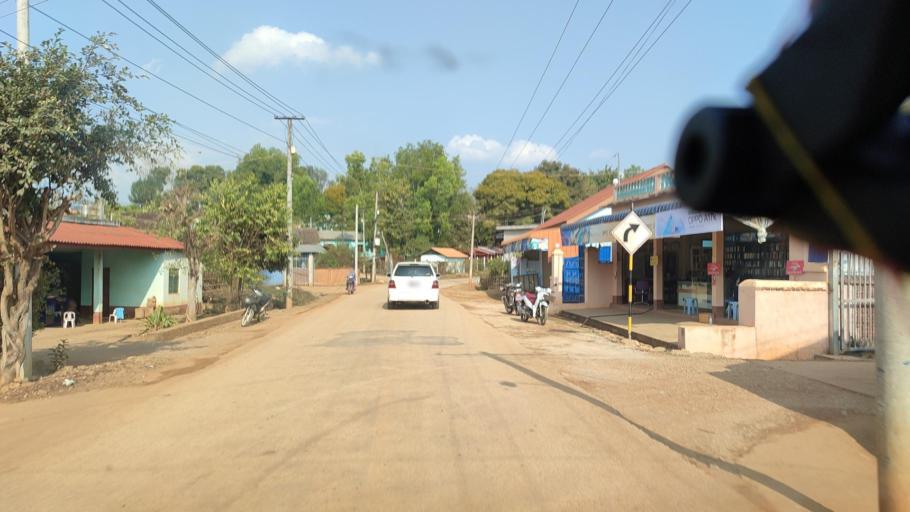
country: CN
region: Yunnan
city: Nayun
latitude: 21.8452
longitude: 99.6895
